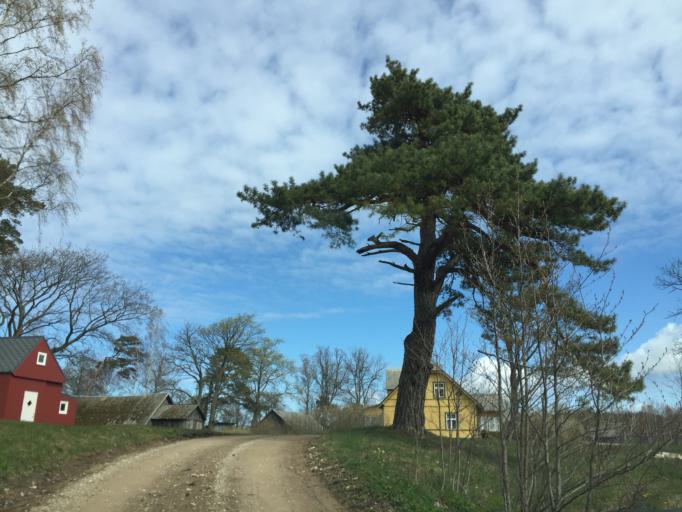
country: LV
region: Salacgrivas
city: Salacgriva
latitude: 57.5882
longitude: 24.3705
